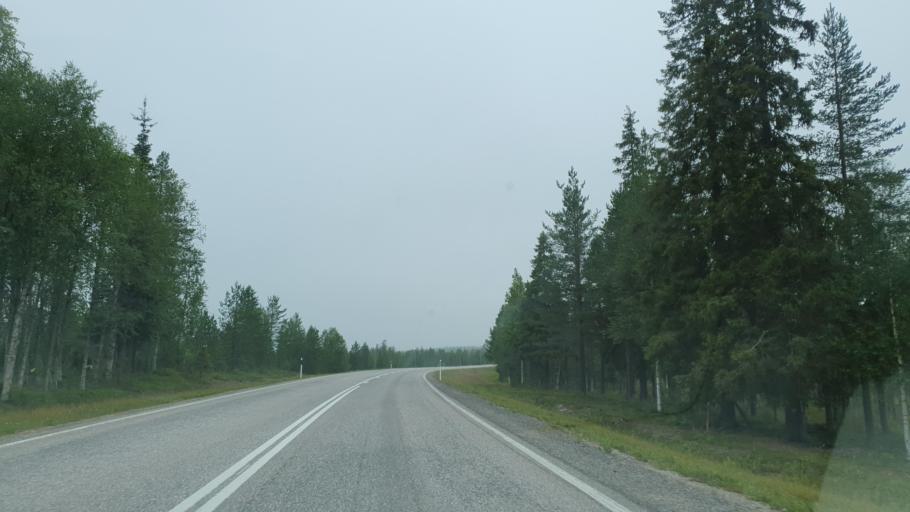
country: FI
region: Lapland
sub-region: Itae-Lappi
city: Salla
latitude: 66.3778
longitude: 28.7040
